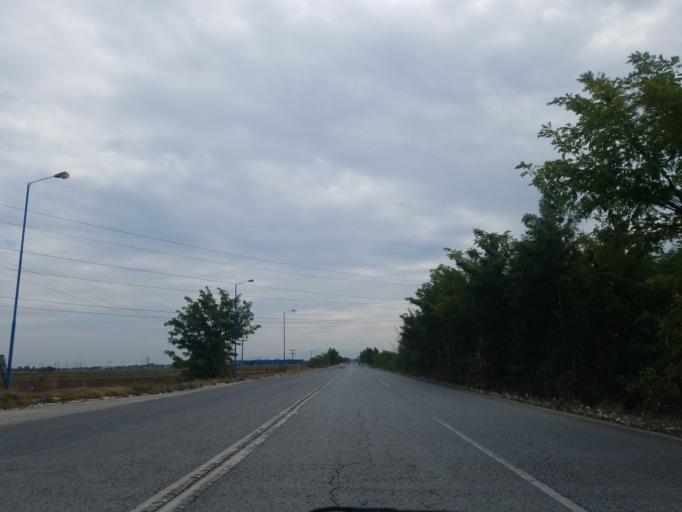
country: GR
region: Thessaly
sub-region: Nomos Kardhitsas
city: Sofades
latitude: 39.3527
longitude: 22.0604
